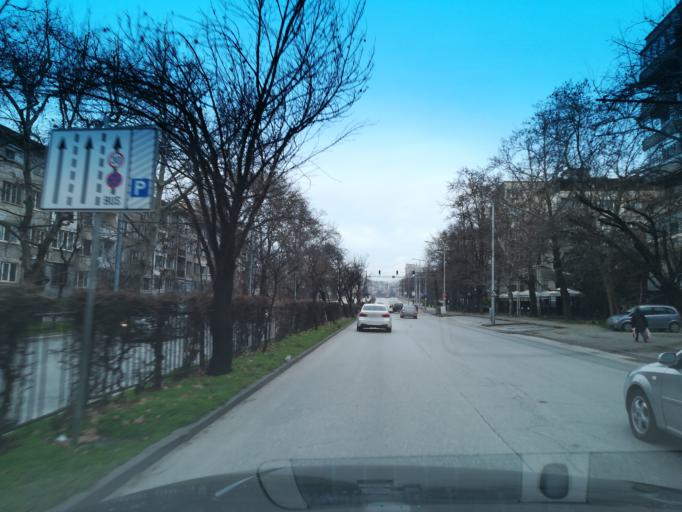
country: BG
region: Plovdiv
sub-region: Obshtina Plovdiv
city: Plovdiv
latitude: 42.1496
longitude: 24.7312
